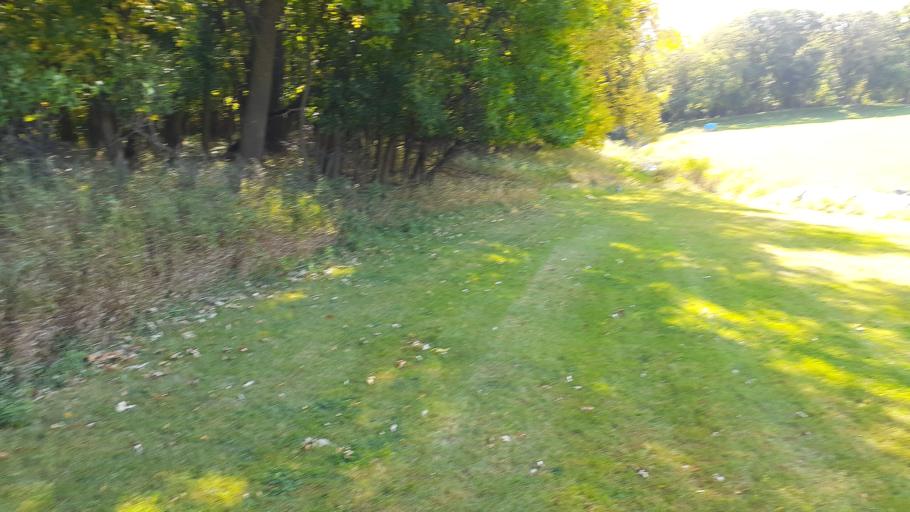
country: US
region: Minnesota
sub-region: Clay County
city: Oakport
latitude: 46.9153
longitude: -96.7656
